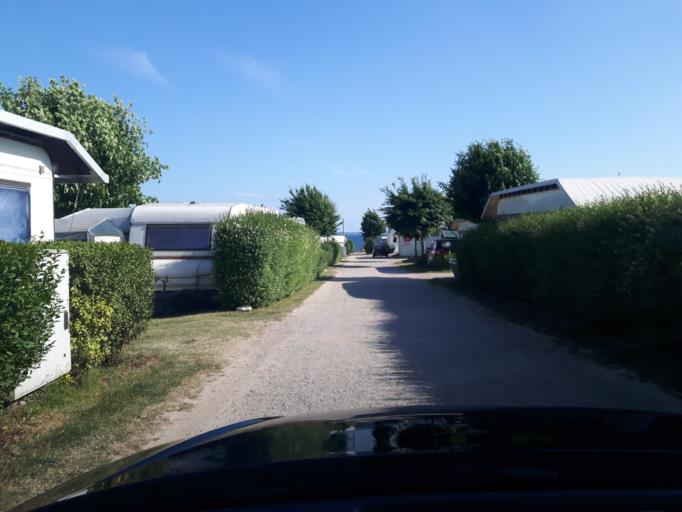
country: DE
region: Schleswig-Holstein
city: Neustadt in Holstein
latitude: 54.0905
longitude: 10.8475
